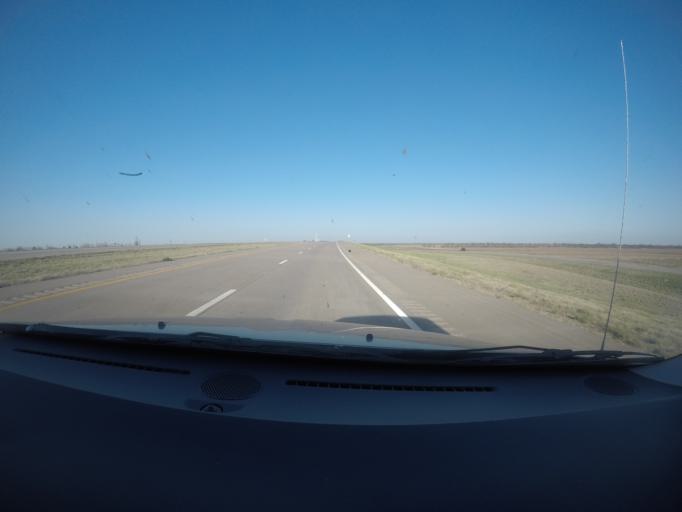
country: US
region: Kansas
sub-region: McPherson County
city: McPherson
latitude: 38.3271
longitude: -97.7008
